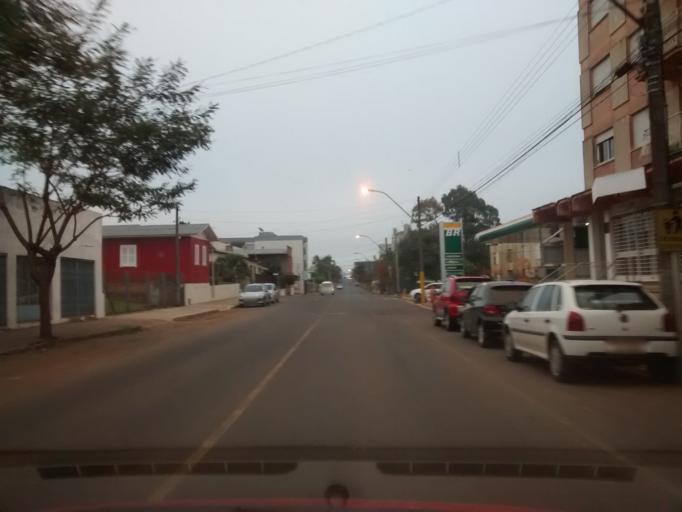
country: BR
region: Rio Grande do Sul
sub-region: Vacaria
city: Vacaria
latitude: -28.5045
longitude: -50.9296
